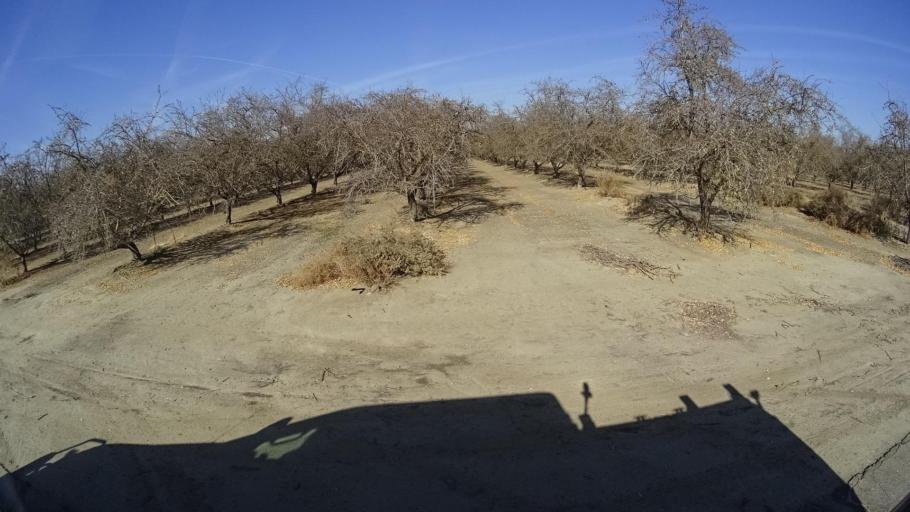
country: US
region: California
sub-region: Kern County
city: Wasco
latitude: 35.6669
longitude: -119.3479
